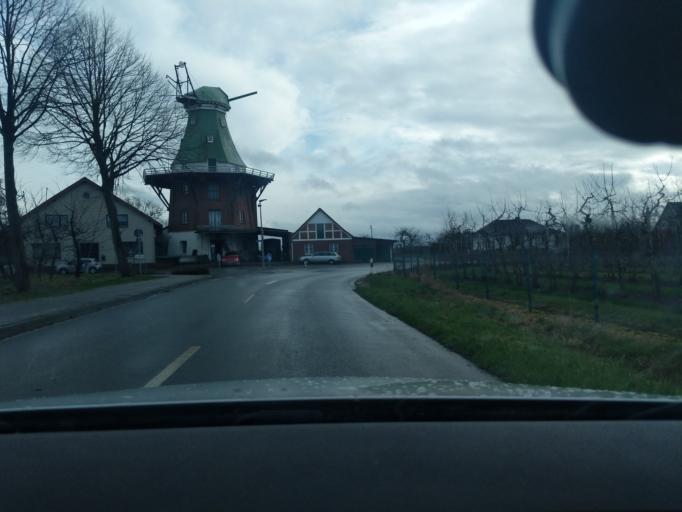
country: DE
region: Schleswig-Holstein
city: Haseldorf
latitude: 53.6017
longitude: 9.5562
